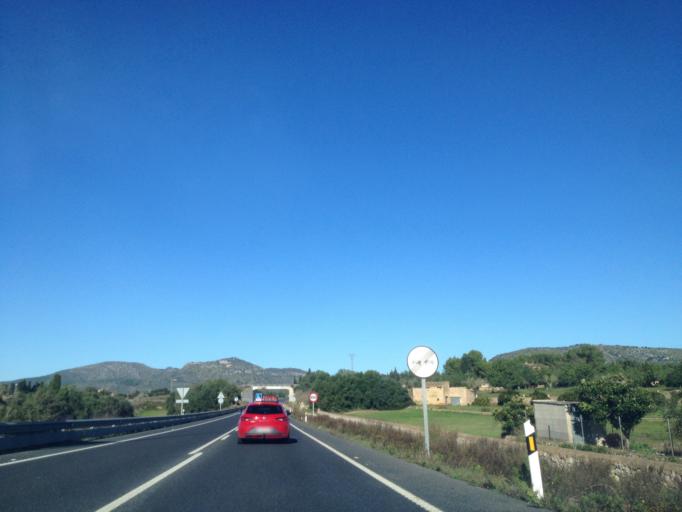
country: ES
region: Balearic Islands
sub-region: Illes Balears
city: Sant Llorenc des Cardassar
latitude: 39.6106
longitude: 3.2988
